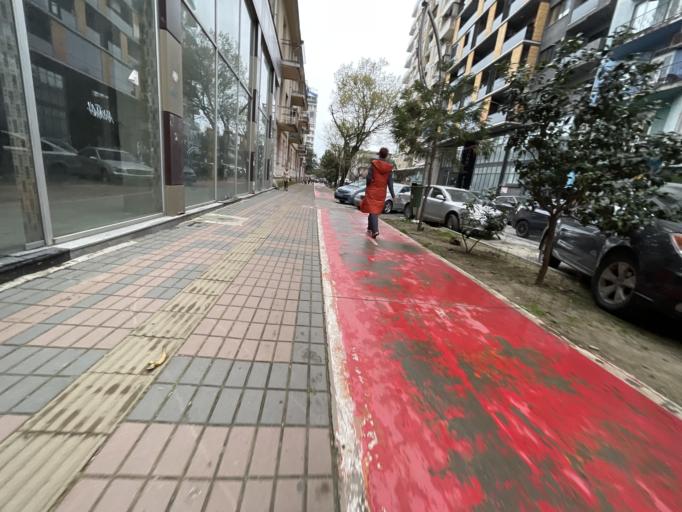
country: GE
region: Ajaria
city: Batumi
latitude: 41.6436
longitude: 41.6288
